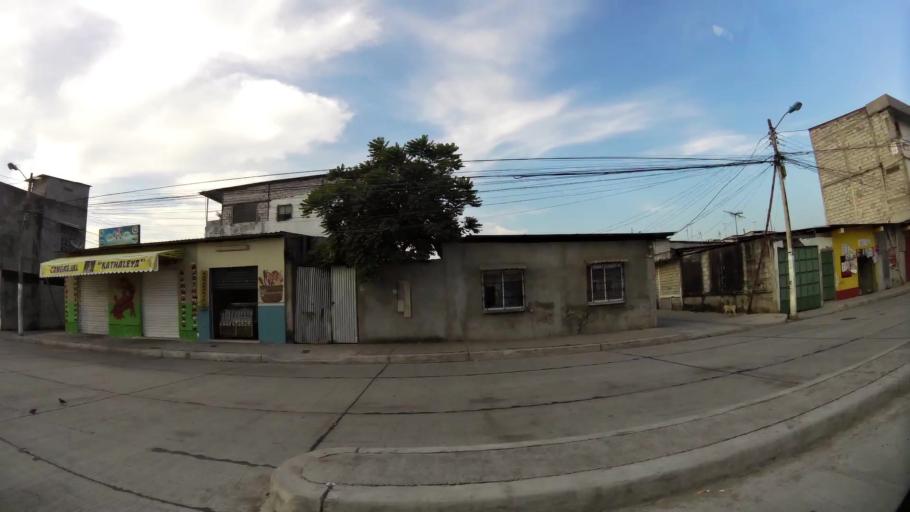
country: EC
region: Guayas
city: Eloy Alfaro
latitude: -2.0886
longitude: -79.9056
